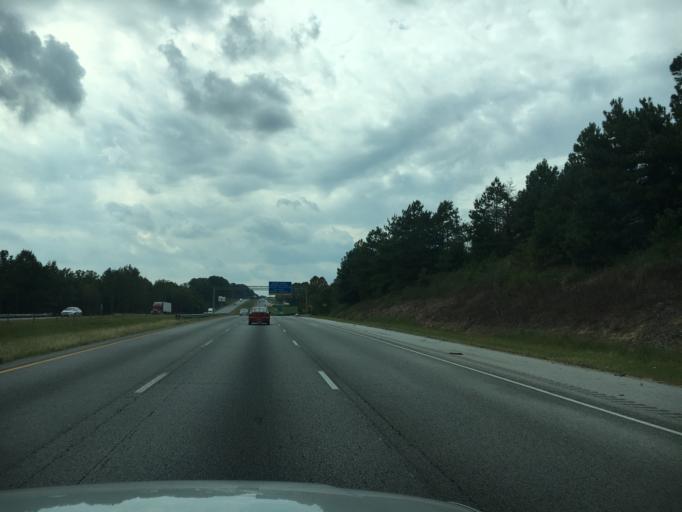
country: US
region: Georgia
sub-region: Franklin County
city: Gumlog
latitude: 34.4718
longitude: -83.0649
